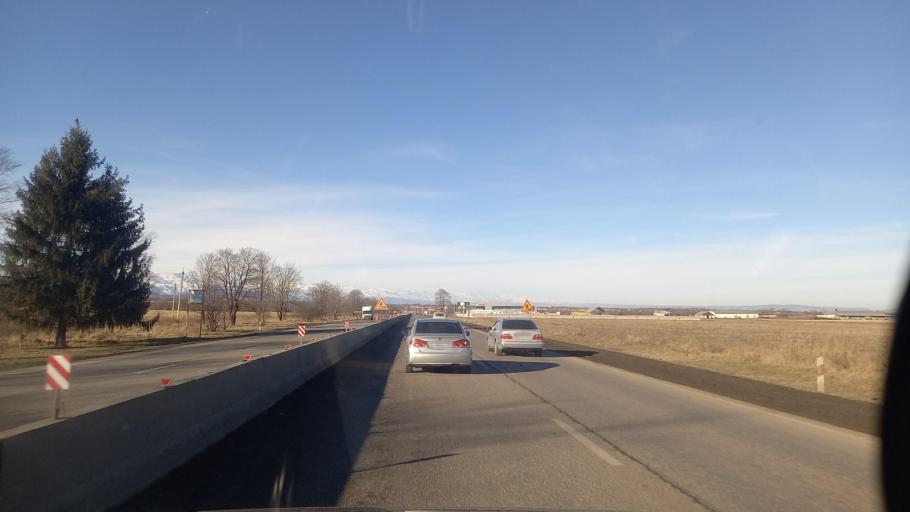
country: RU
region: North Ossetia
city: Vladikavkaz
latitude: 43.0259
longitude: 44.6221
